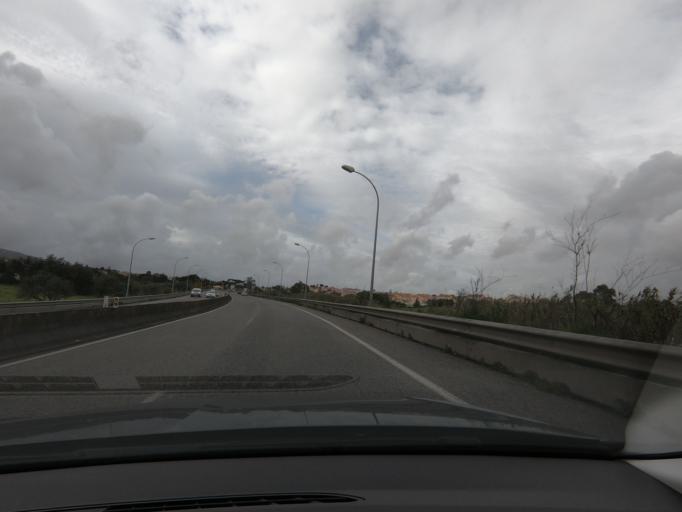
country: PT
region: Lisbon
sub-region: Sintra
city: Rio de Mouro
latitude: 38.7585
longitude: -9.3443
